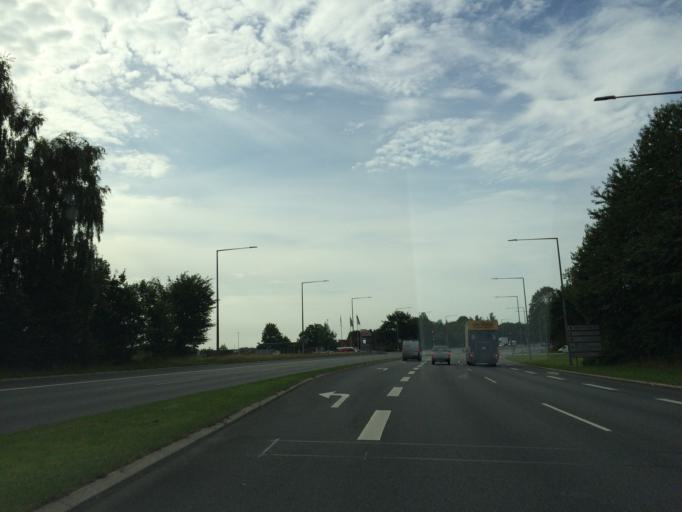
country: DK
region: South Denmark
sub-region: Kolding Kommune
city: Kolding
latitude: 55.5085
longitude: 9.5044
